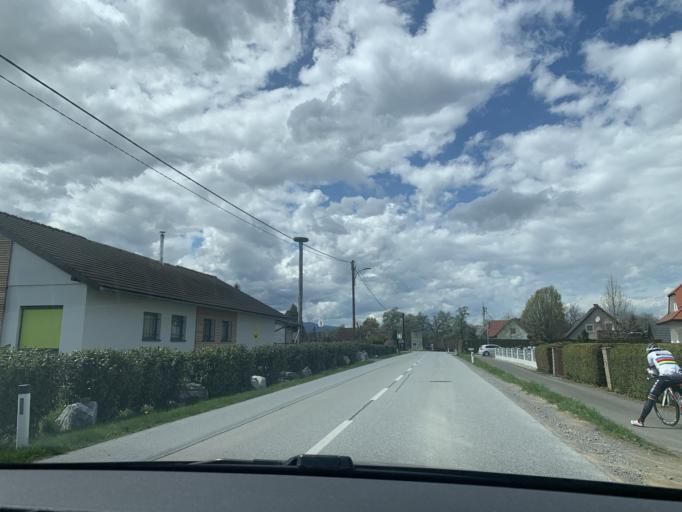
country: AT
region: Styria
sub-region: Politischer Bezirk Graz-Umgebung
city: Wundschuh
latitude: 46.9073
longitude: 15.4176
